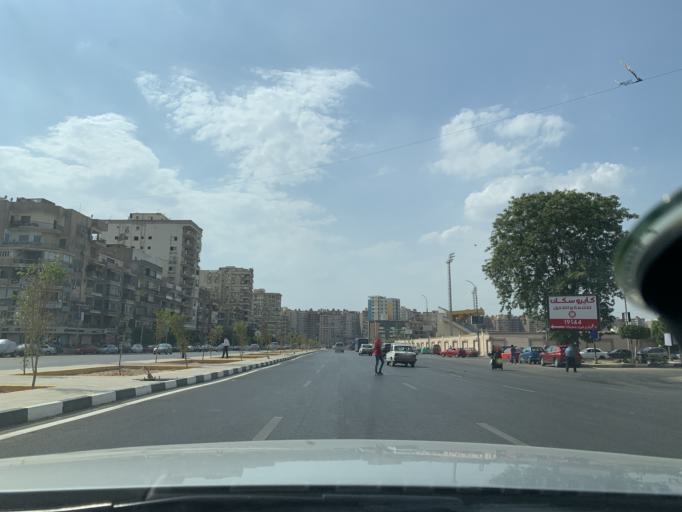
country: EG
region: Muhafazat al Qalyubiyah
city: Al Khankah
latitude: 30.1144
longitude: 31.3438
